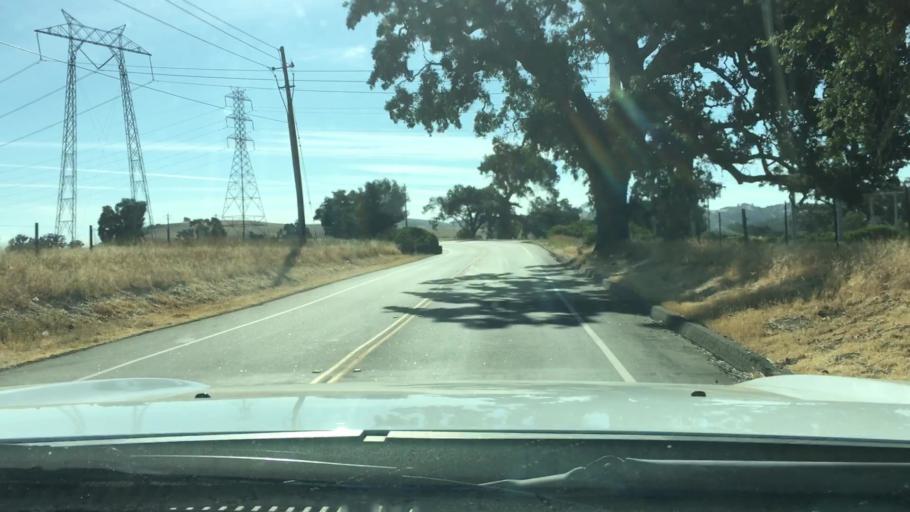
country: US
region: California
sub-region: San Luis Obispo County
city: Templeton
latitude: 35.5568
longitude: -120.6819
